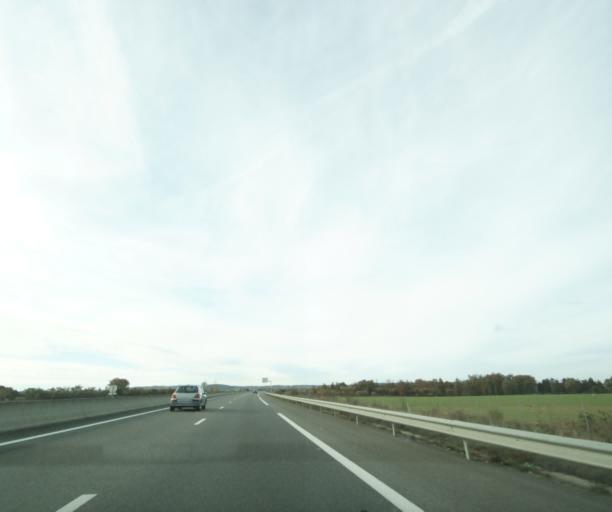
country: FR
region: Midi-Pyrenees
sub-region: Departement de la Haute-Garonne
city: Leguevin
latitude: 43.5813
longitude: 1.2260
